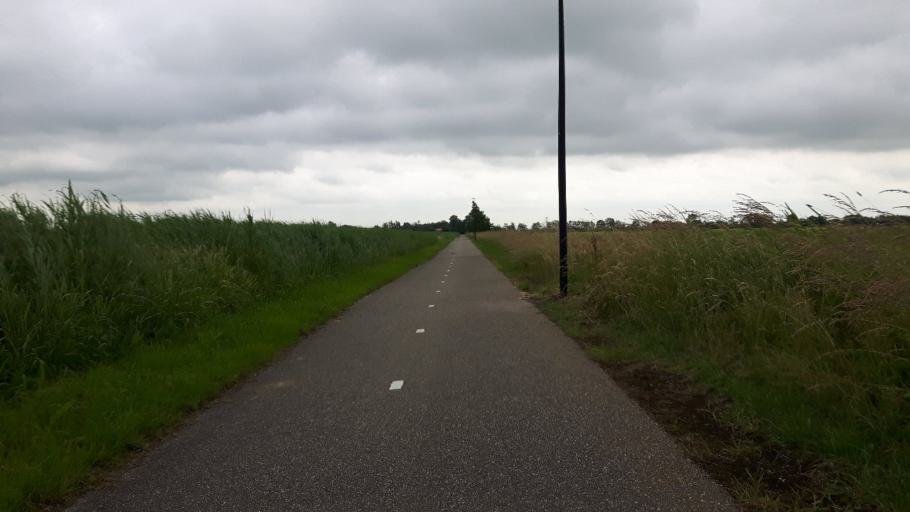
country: NL
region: Utrecht
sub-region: Gemeente Oudewater
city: Oudewater
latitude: 52.0612
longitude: 4.8394
